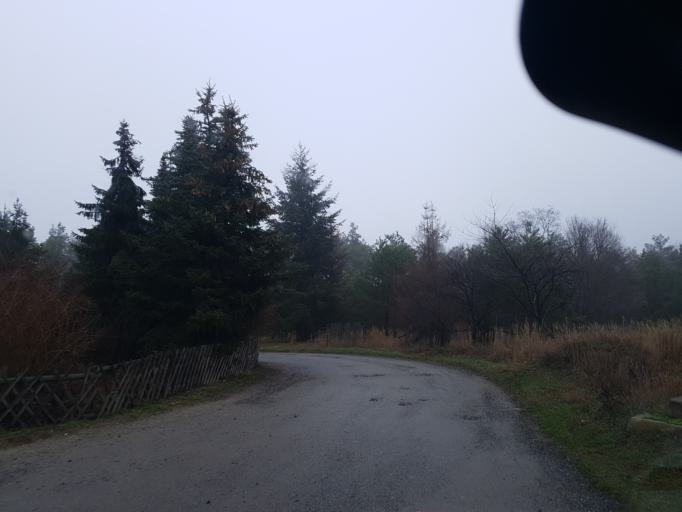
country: DE
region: Brandenburg
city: Finsterwalde
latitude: 51.6505
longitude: 13.7025
